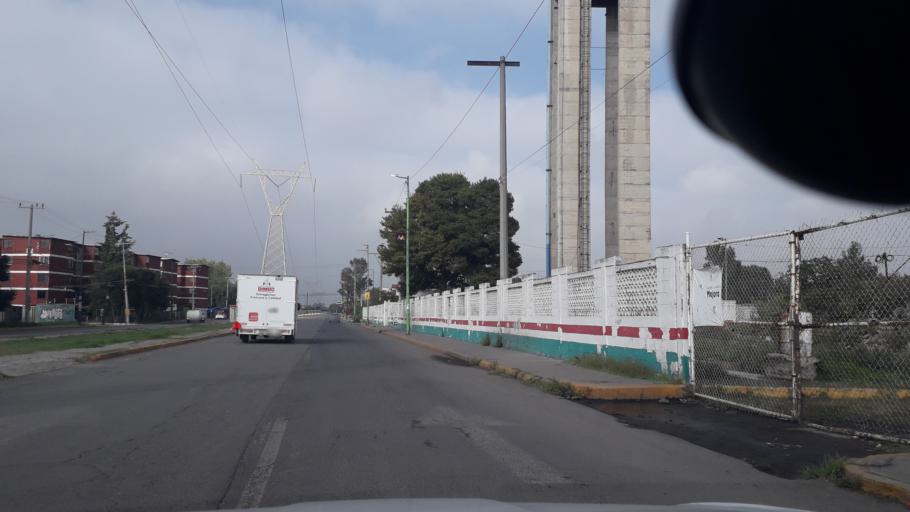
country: MX
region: Mexico
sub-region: Jaltenco
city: Alborada Jaltenco
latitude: 19.6449
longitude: -99.0780
